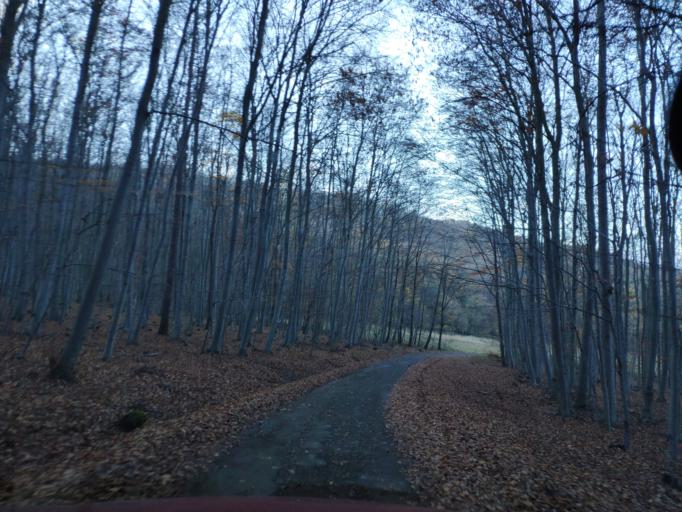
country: SK
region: Kosicky
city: Secovce
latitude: 48.5853
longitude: 21.5057
